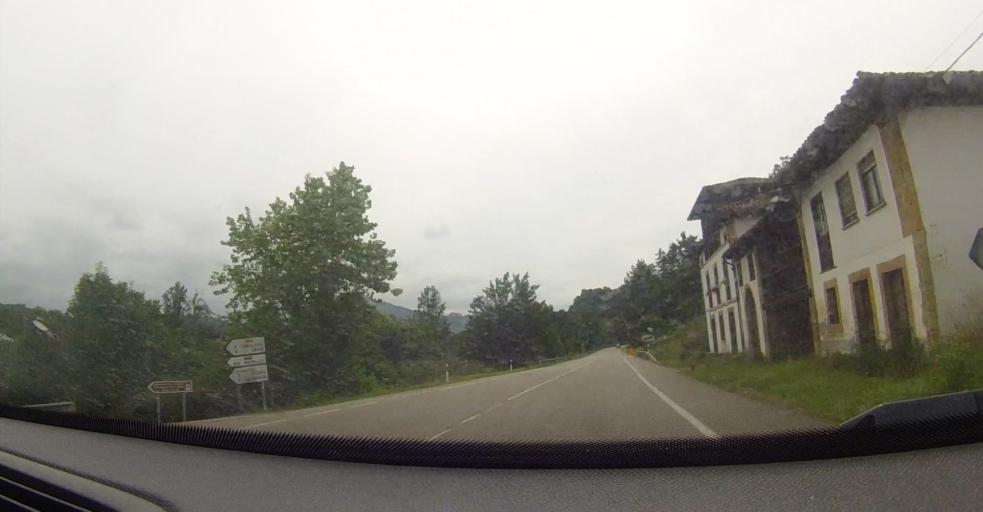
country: ES
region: Asturias
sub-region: Province of Asturias
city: Parres
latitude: 43.3685
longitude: -5.1862
